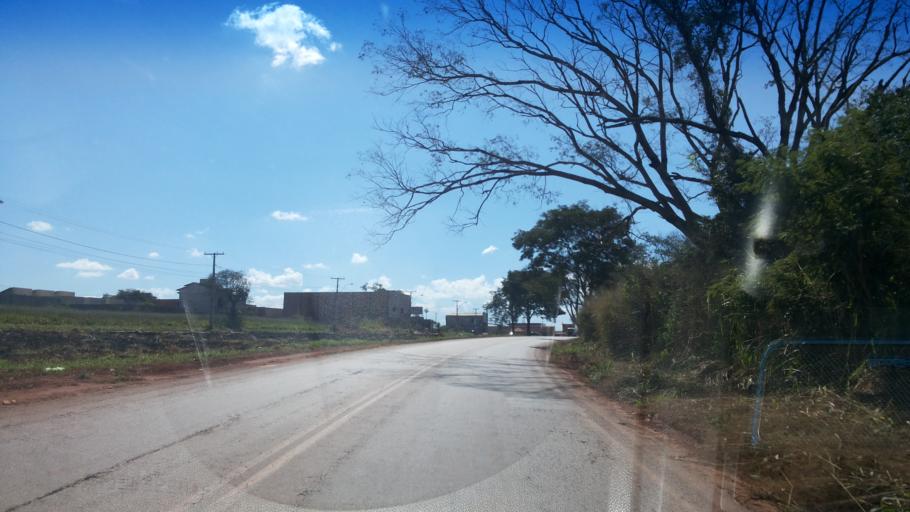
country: BR
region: Goias
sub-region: Goiania
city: Goiania
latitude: -16.5587
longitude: -49.2684
